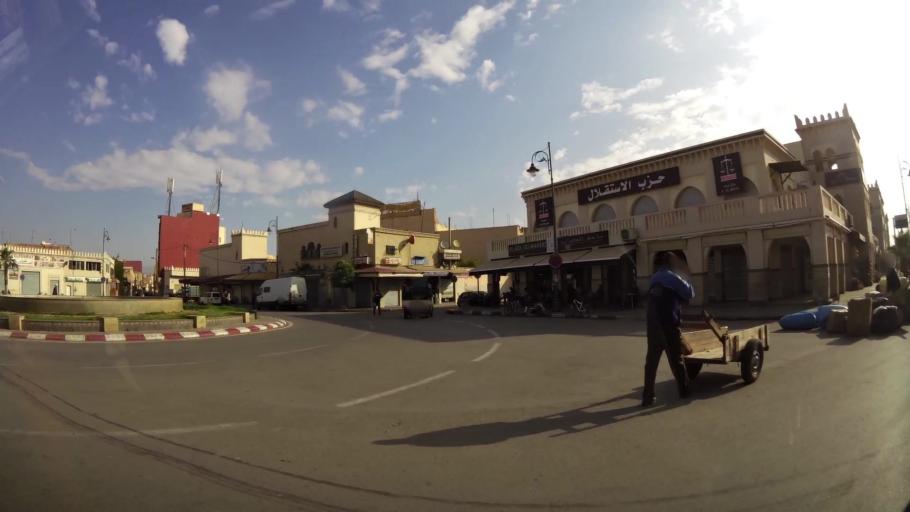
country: MA
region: Oriental
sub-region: Oujda-Angad
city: Oujda
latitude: 34.6815
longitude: -1.9106
